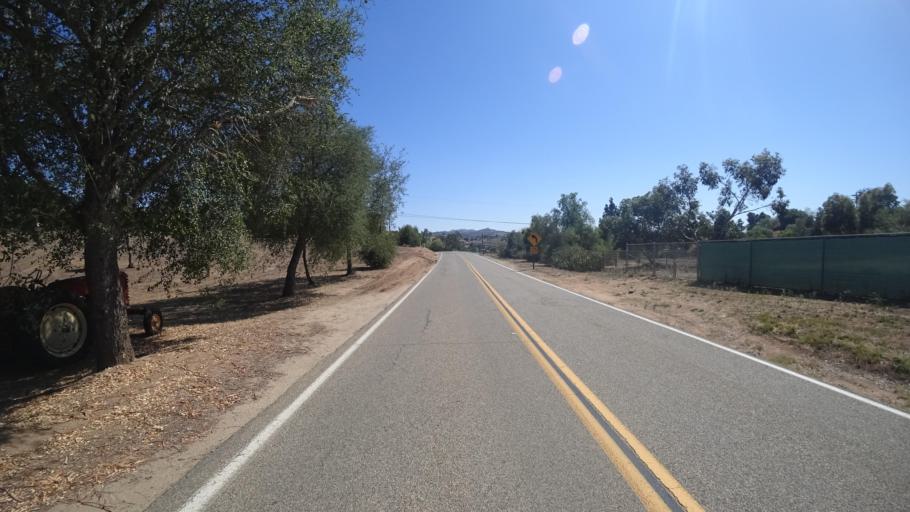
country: US
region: California
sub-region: San Diego County
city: Hidden Meadows
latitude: 33.2866
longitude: -117.1211
